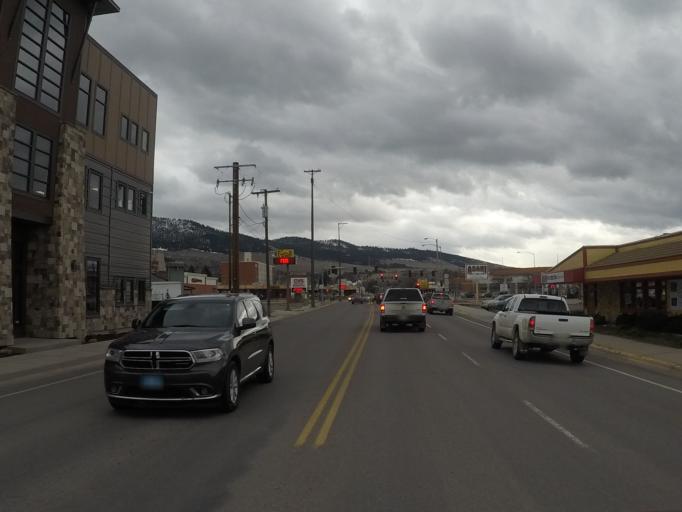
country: US
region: Montana
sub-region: Missoula County
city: Missoula
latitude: 46.8533
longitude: -114.0131
